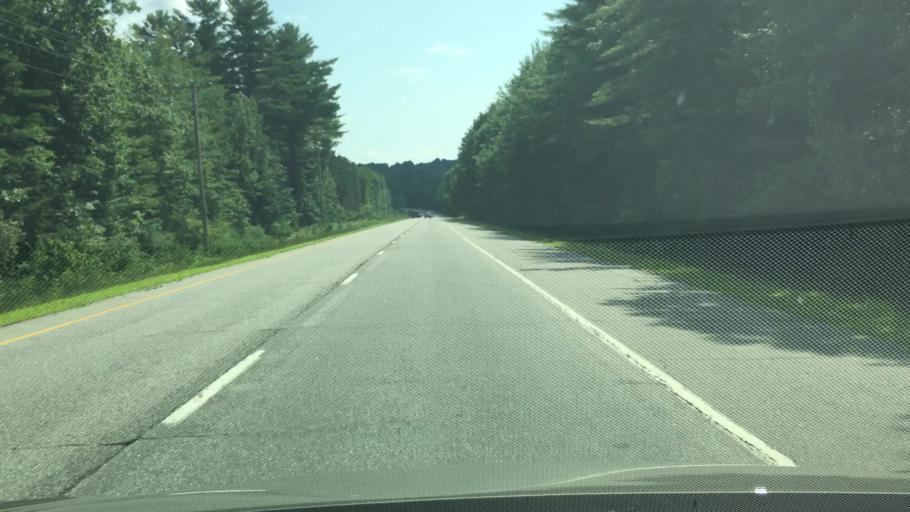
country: US
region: Maine
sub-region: Androscoggin County
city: Auburn
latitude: 44.0648
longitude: -70.2518
